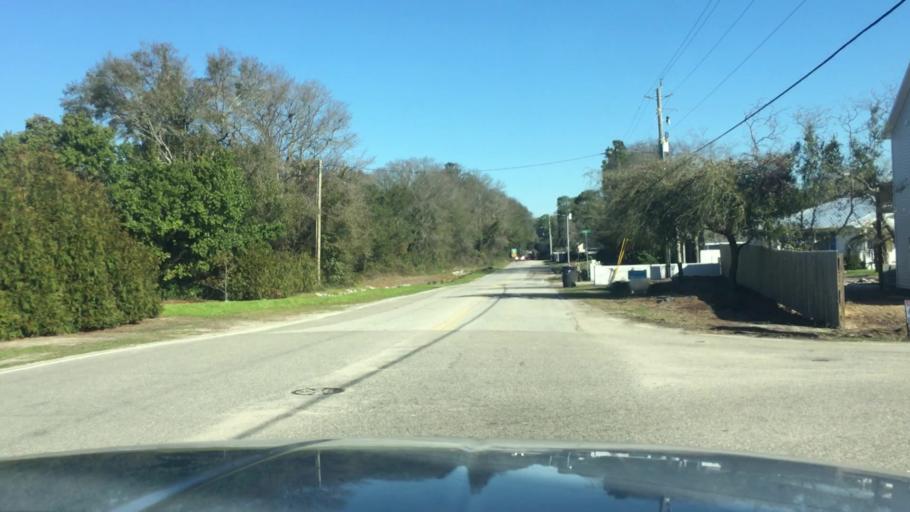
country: US
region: North Carolina
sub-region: New Hanover County
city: Sea Breeze
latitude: 34.0513
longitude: -77.8995
